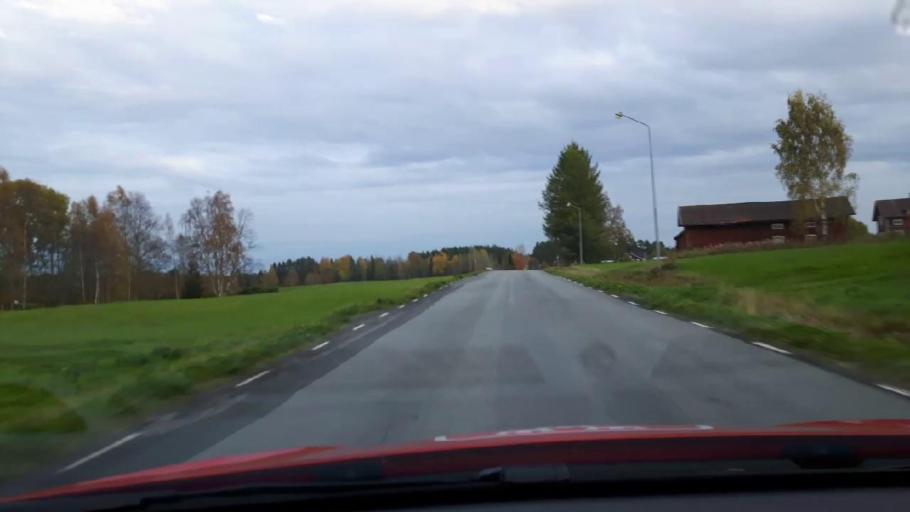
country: SE
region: Jaemtland
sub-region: OEstersunds Kommun
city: Lit
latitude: 63.3133
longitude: 14.9887
